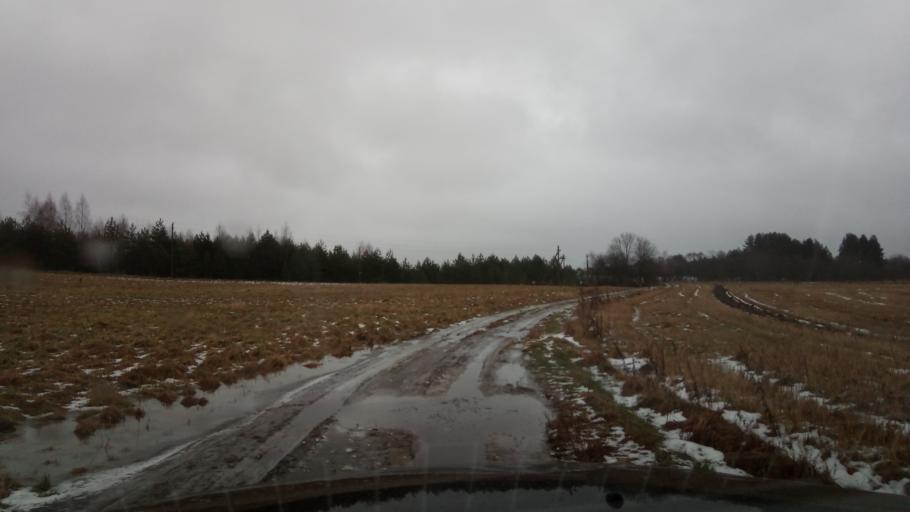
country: LT
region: Utenos apskritis
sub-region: Utena
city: Utena
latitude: 55.3700
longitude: 25.7618
